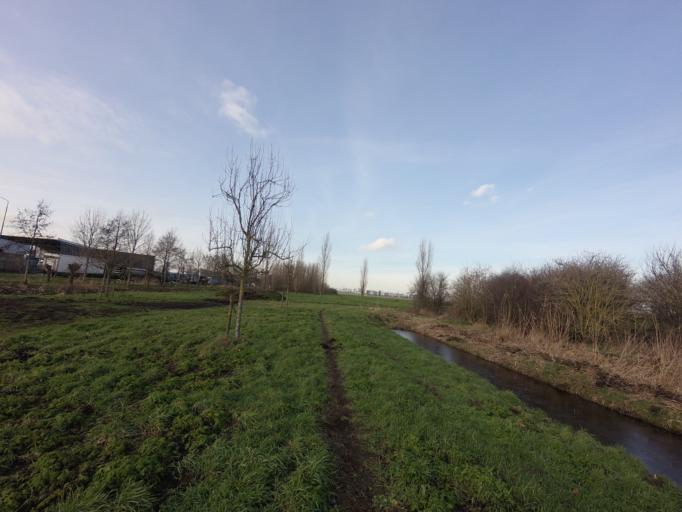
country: NL
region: Utrecht
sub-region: Gemeente Oudewater
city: Oudewater
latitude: 52.0345
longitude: 4.8715
